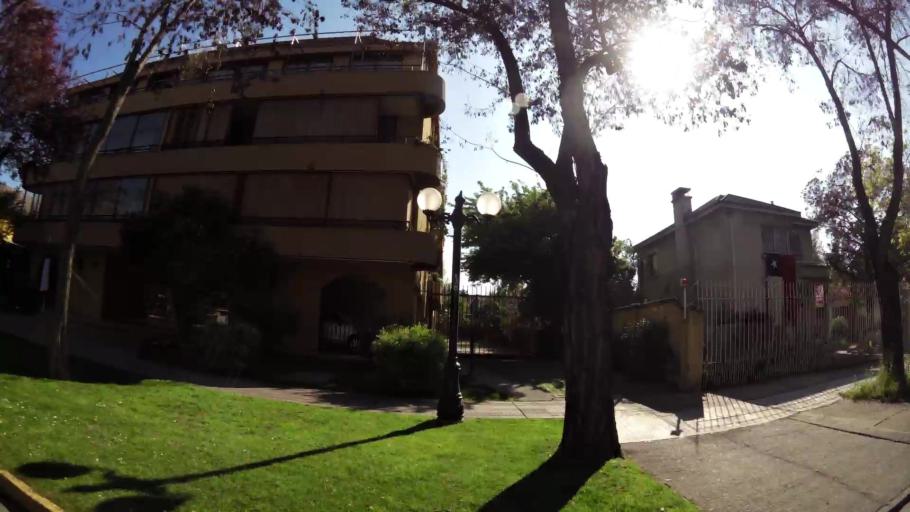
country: CL
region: Santiago Metropolitan
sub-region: Provincia de Santiago
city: Villa Presidente Frei, Nunoa, Santiago, Chile
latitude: -33.4383
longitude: -70.5889
